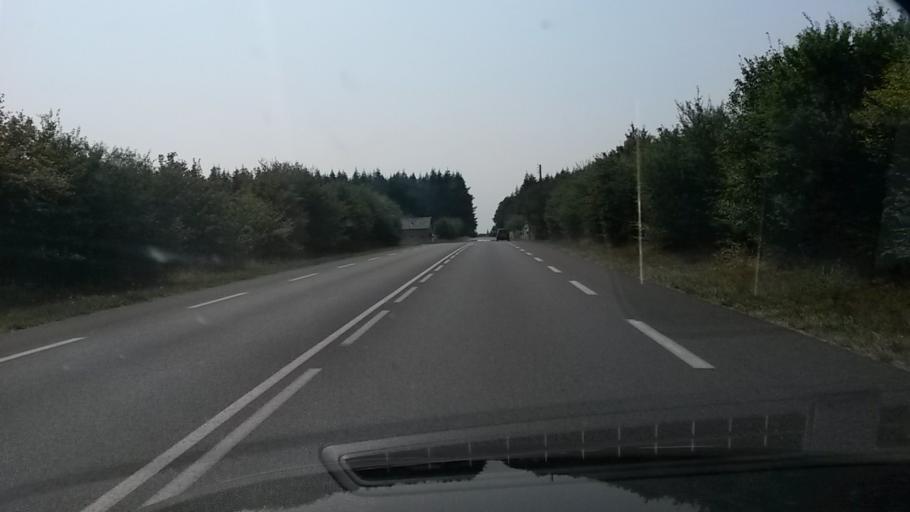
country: FR
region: Pays de la Loire
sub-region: Departement de la Mayenne
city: Saint-Fort
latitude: 47.8028
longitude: -0.7486
